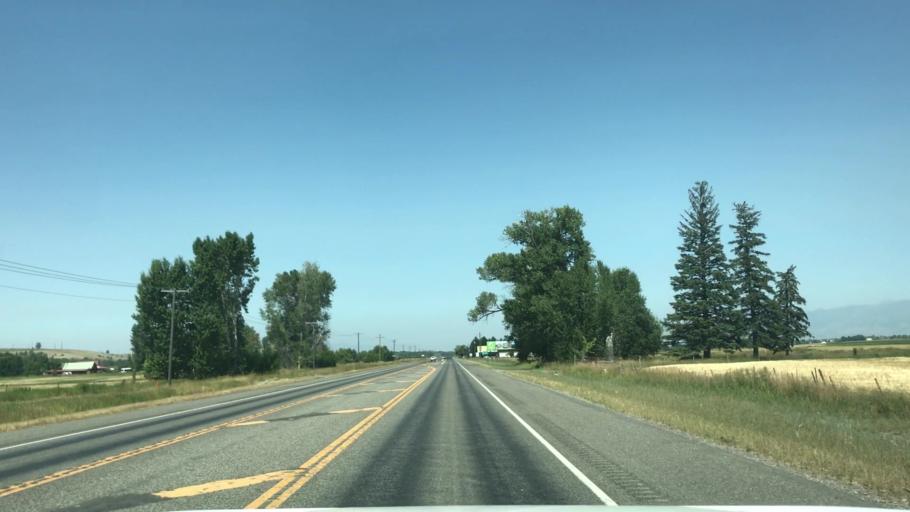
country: US
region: Montana
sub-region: Gallatin County
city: Four Corners
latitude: 45.6207
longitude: -111.1969
